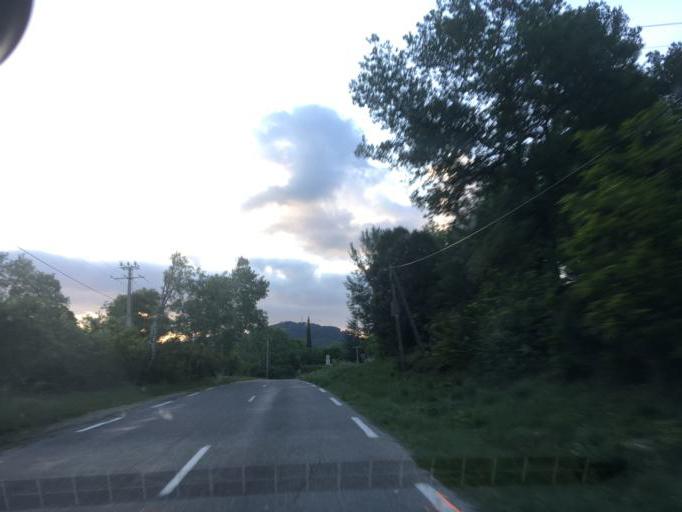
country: FR
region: Provence-Alpes-Cote d'Azur
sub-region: Departement du Var
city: Salernes
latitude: 43.5487
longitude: 6.2471
